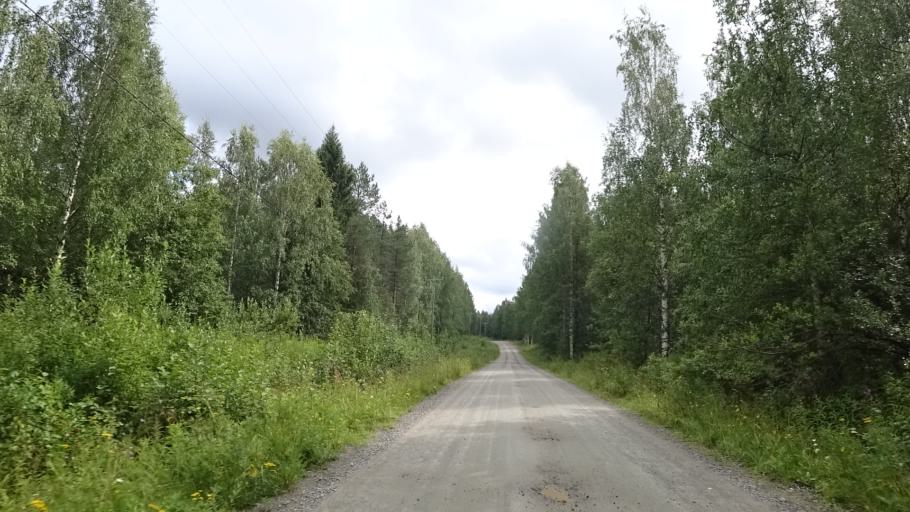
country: FI
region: North Karelia
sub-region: Joensuu
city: Ilomantsi
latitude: 62.9313
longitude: 31.3103
